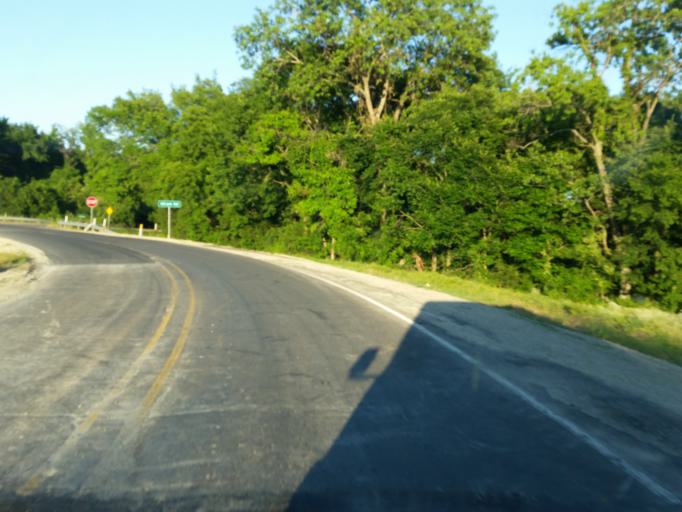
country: US
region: Texas
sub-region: Van Zandt County
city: Wills Point
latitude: 32.6670
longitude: -96.1461
